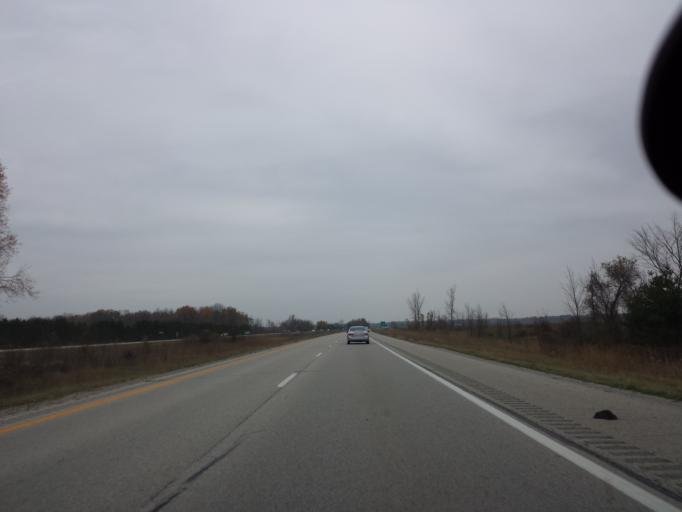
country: US
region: Michigan
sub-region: Arenac County
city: Standish
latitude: 43.9606
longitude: -84.0157
